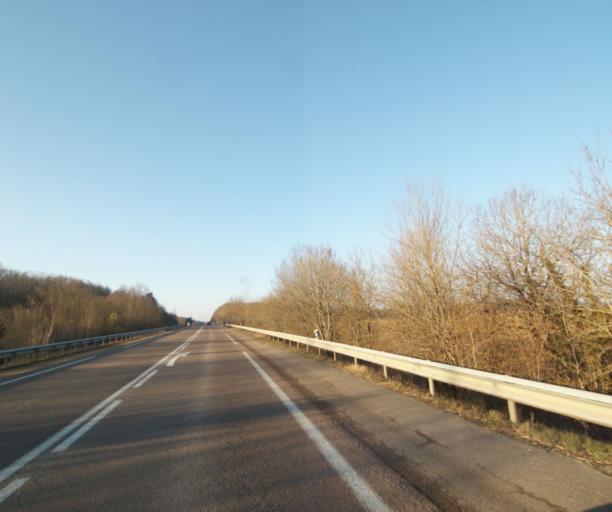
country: FR
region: Champagne-Ardenne
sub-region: Departement de la Haute-Marne
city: Chevillon
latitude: 48.4997
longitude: 5.1075
